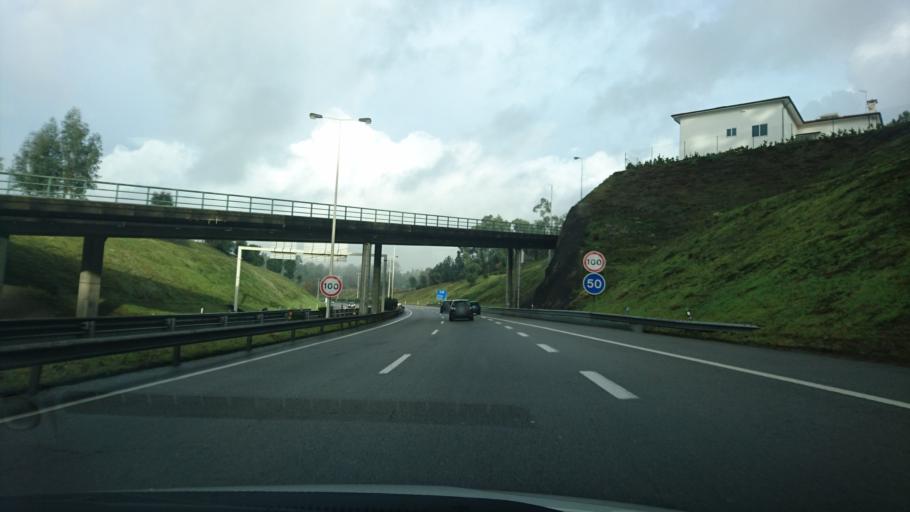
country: PT
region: Porto
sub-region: Gondomar
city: Gondomar
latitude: 41.1515
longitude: -8.5485
